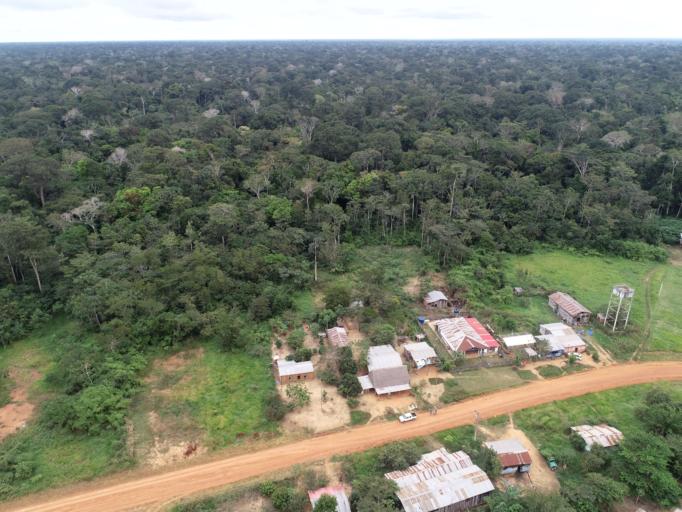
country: PE
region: Madre de Dios
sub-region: Provincia de Tambopata
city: Puerto Maldonado
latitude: -12.1979
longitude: -68.6329
